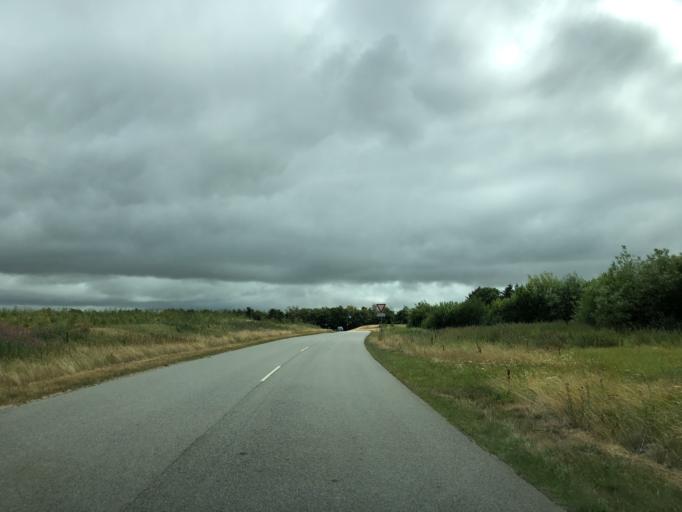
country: DK
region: Central Jutland
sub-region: Herning Kommune
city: Vildbjerg
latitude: 56.1844
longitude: 8.7551
